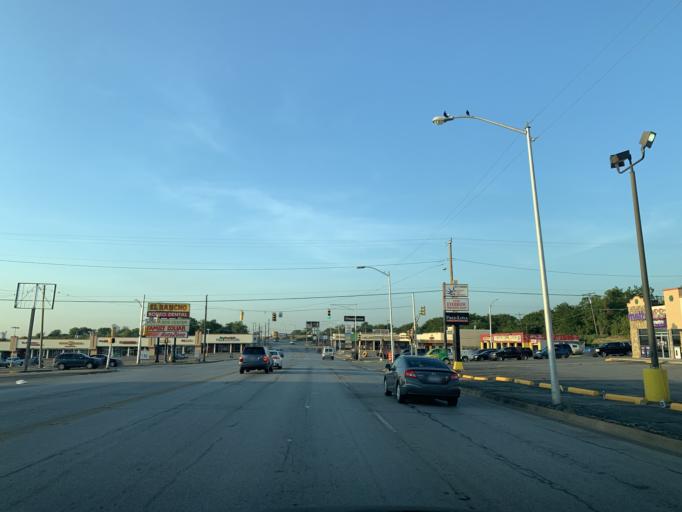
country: US
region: Texas
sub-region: Tarrant County
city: River Oaks
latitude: 32.8054
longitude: -97.3516
